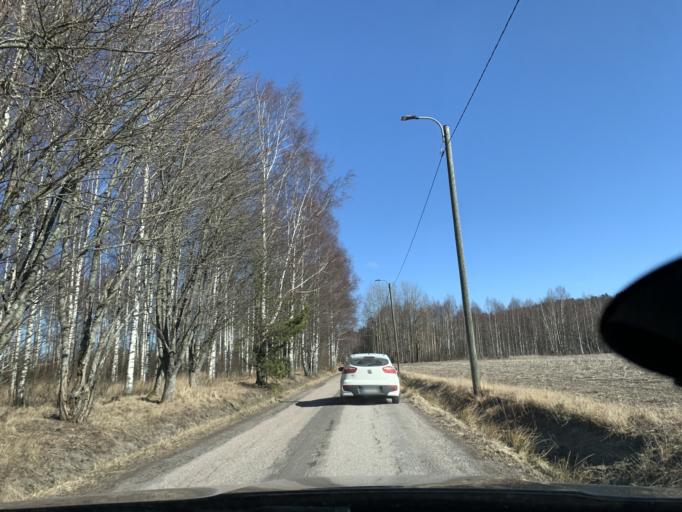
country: FI
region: Uusimaa
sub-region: Helsinki
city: Espoo
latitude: 60.1747
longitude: 24.5835
